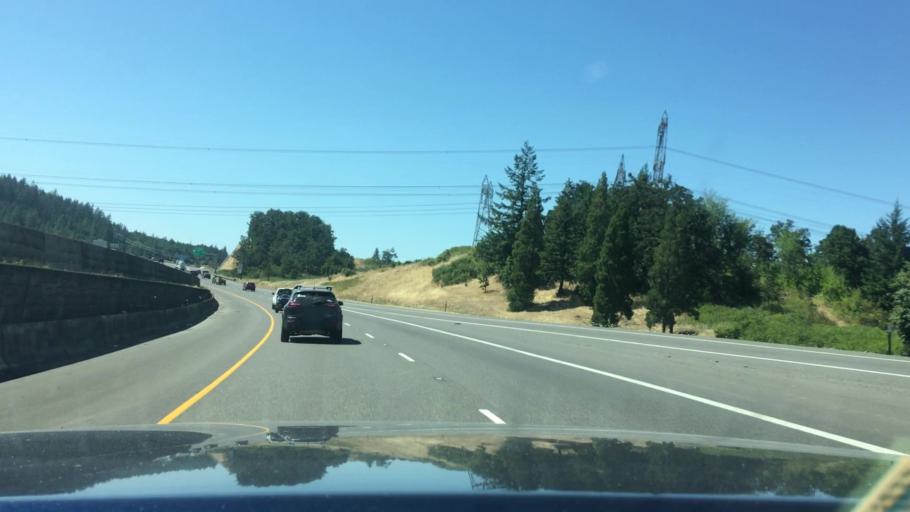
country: US
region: Oregon
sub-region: Lane County
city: Springfield
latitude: 43.9983
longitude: -123.0080
